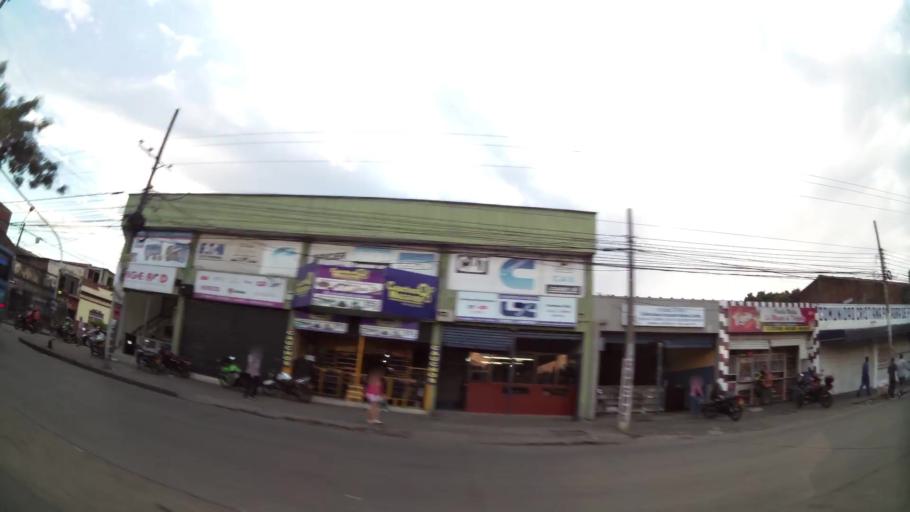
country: CO
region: Valle del Cauca
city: Cali
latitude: 3.4609
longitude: -76.5140
